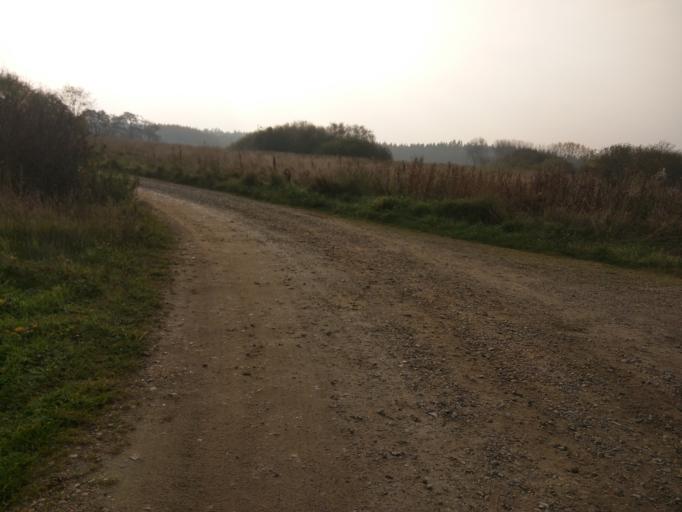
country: DK
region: Central Jutland
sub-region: Viborg Kommune
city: Viborg
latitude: 56.4395
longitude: 9.3582
